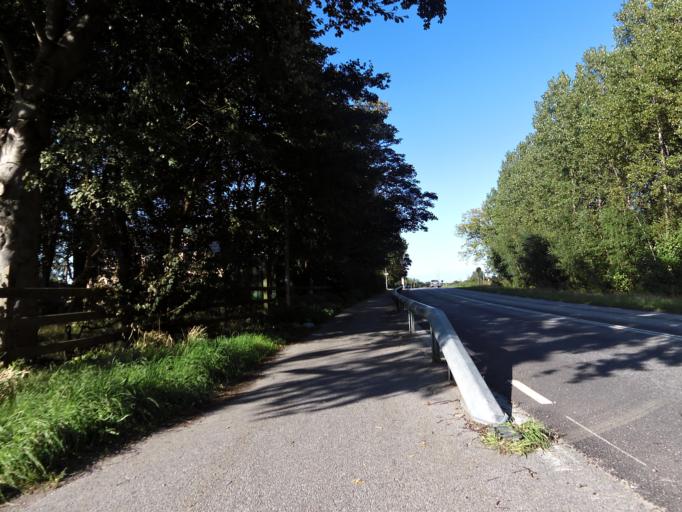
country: SE
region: Skane
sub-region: Lomma Kommun
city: Lomma
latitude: 55.6560
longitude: 13.0561
